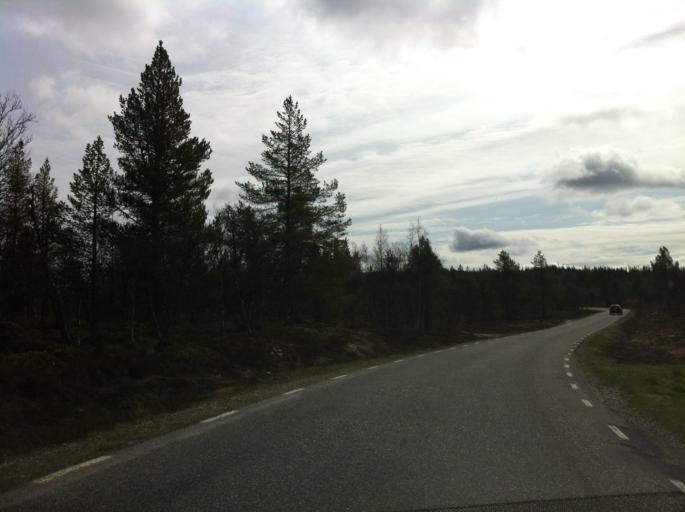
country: NO
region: Hedmark
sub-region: Engerdal
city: Engerdal
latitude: 62.3208
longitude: 12.8088
